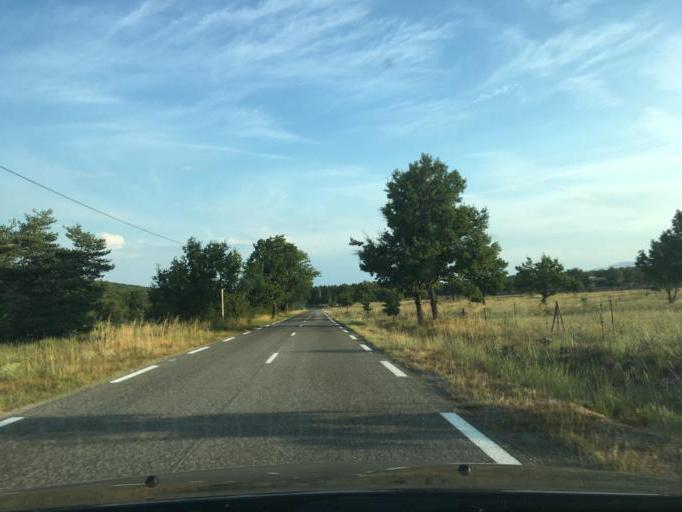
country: FR
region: Provence-Alpes-Cote d'Azur
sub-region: Departement du Var
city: Aups
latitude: 43.6883
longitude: 6.2223
